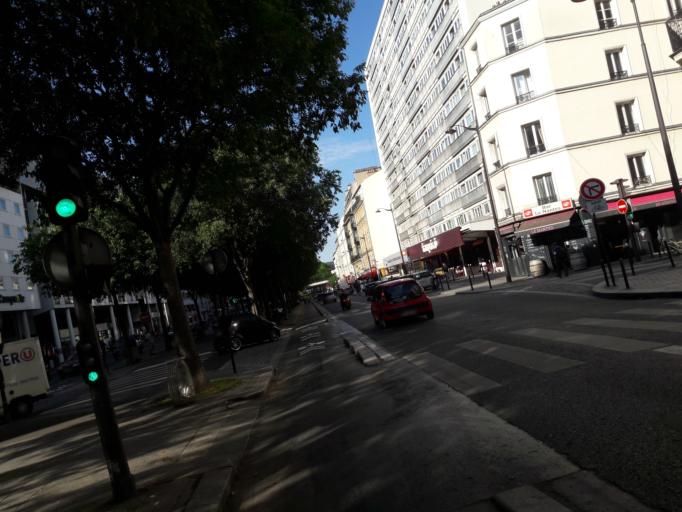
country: FR
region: Ile-de-France
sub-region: Departement de Seine-Saint-Denis
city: Aubervilliers
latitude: 48.8929
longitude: 2.3798
